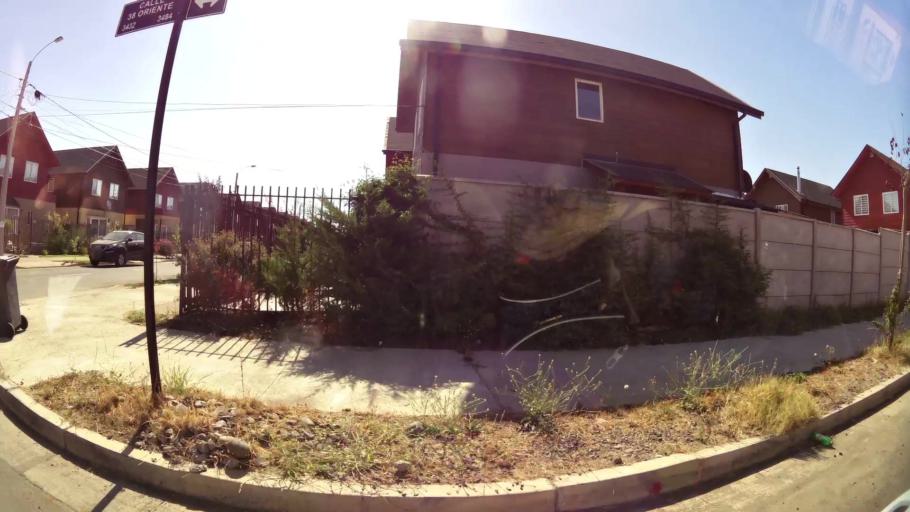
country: CL
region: Maule
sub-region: Provincia de Talca
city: Talca
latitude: -35.4177
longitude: -71.6072
